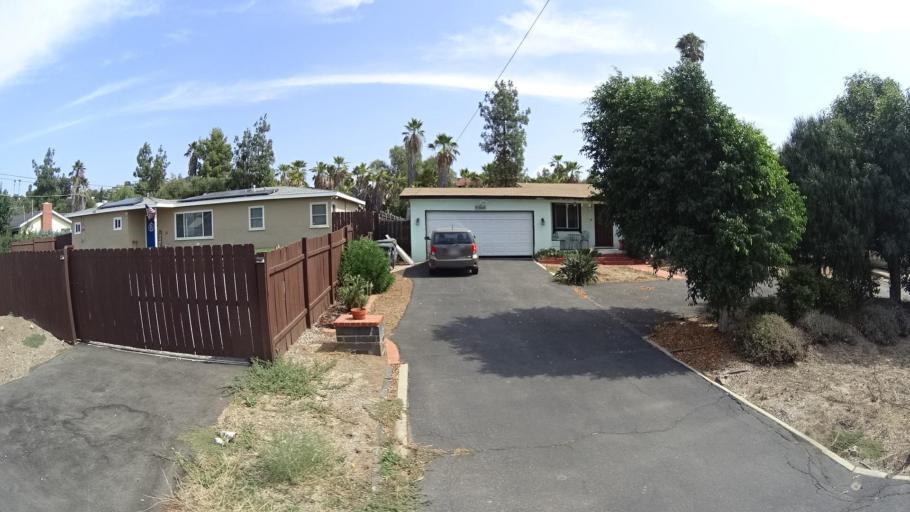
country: US
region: California
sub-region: San Diego County
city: Escondido
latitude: 33.1195
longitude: -117.0424
